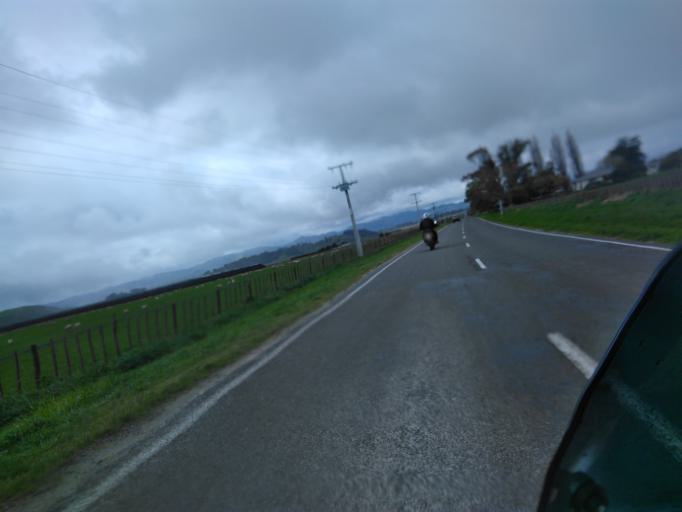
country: NZ
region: Gisborne
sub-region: Gisborne District
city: Gisborne
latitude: -38.6459
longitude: 177.8535
